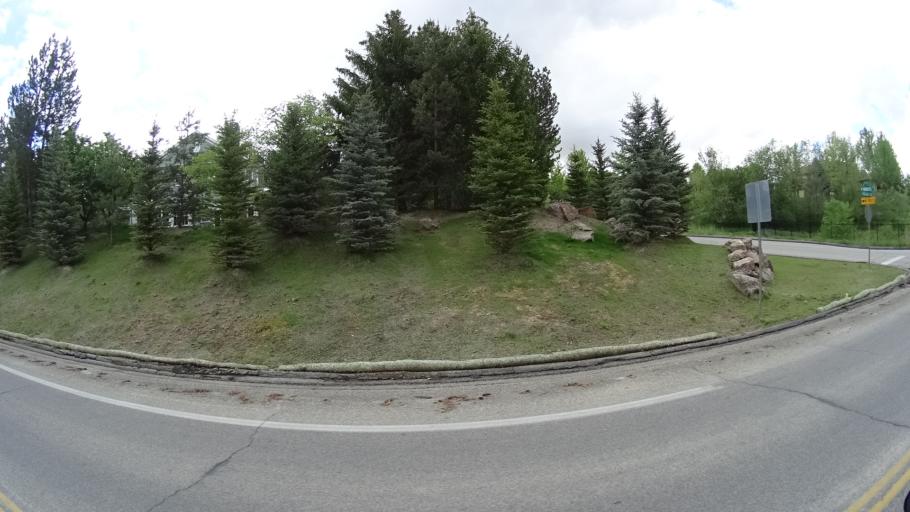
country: US
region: Idaho
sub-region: Ada County
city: Boise
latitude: 43.6434
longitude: -116.2042
